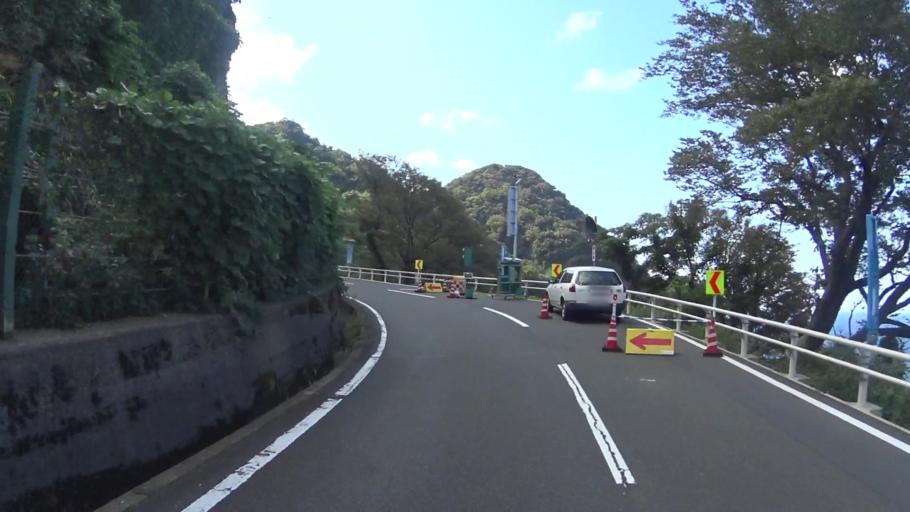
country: JP
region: Kyoto
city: Miyazu
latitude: 35.7676
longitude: 135.2335
